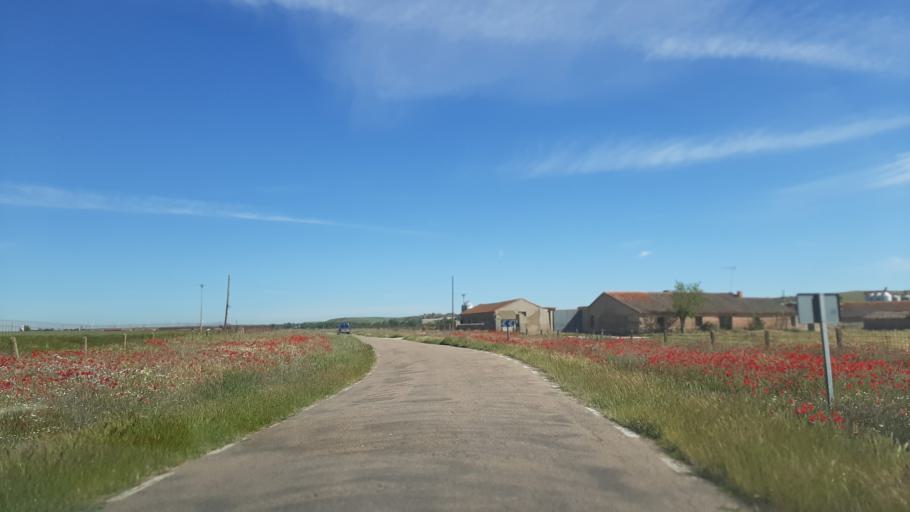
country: ES
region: Castille and Leon
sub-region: Provincia de Salamanca
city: Gajates
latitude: 40.7961
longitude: -5.3728
